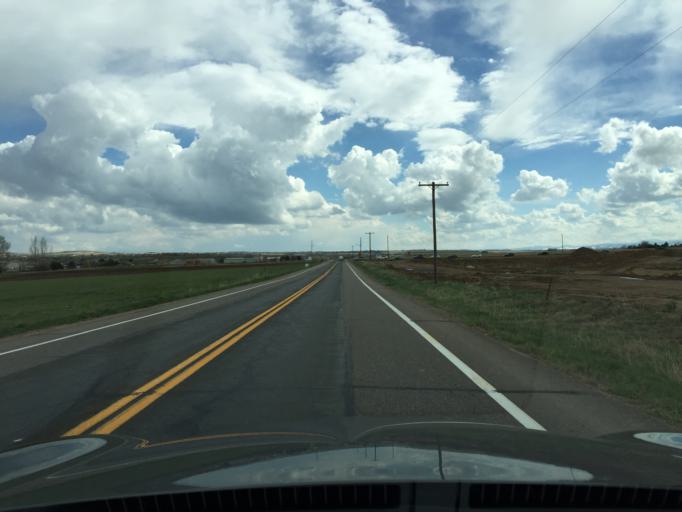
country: US
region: Colorado
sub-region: Boulder County
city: Erie
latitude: 40.0170
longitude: -105.0554
